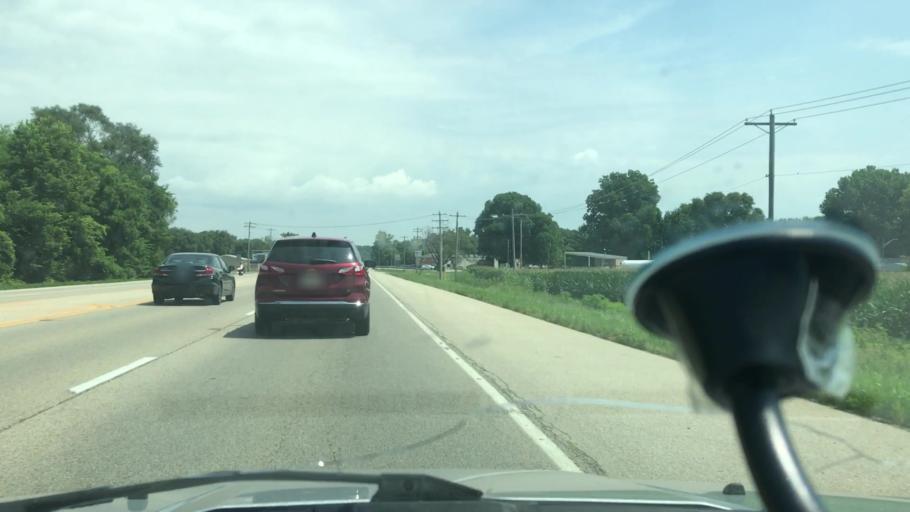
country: US
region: Illinois
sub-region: Tazewell County
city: North Pekin
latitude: 40.6162
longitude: -89.6285
